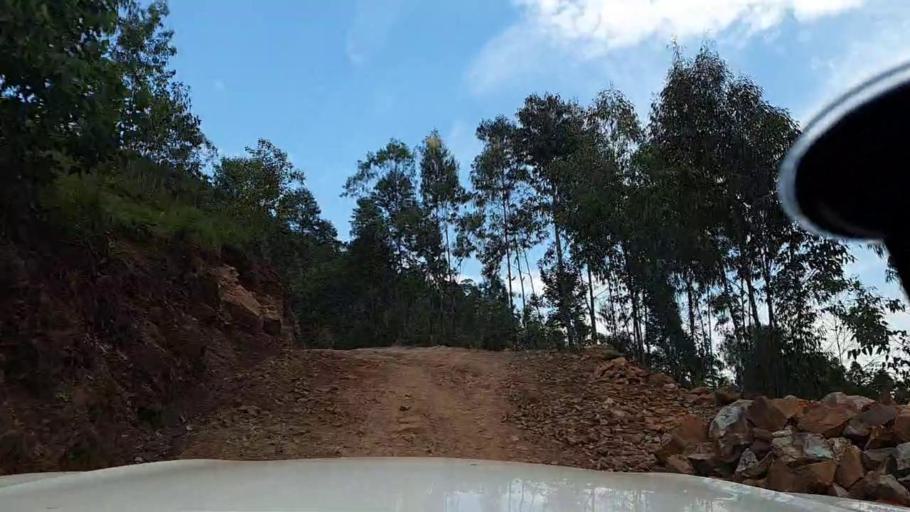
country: RW
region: Southern Province
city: Gitarama
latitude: -1.8051
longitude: 29.7976
